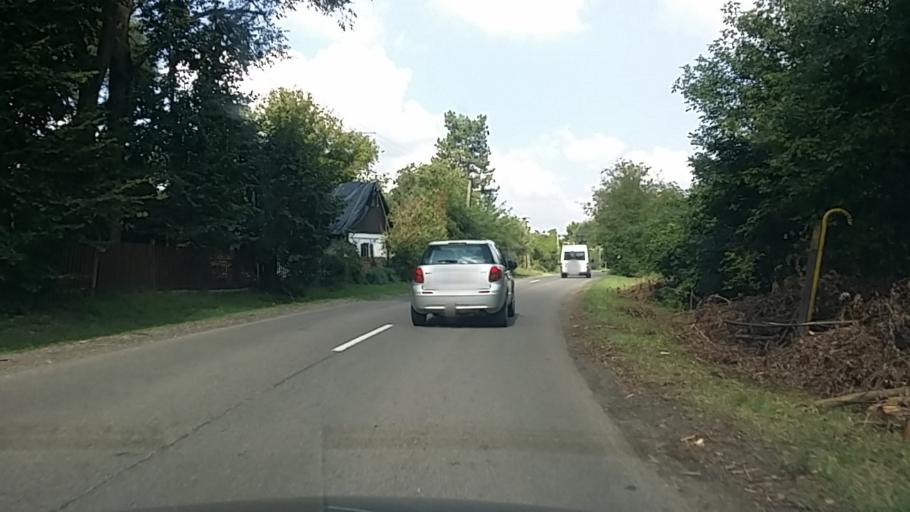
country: HU
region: Bacs-Kiskun
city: Tiszaalpar
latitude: 46.8428
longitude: 19.9777
